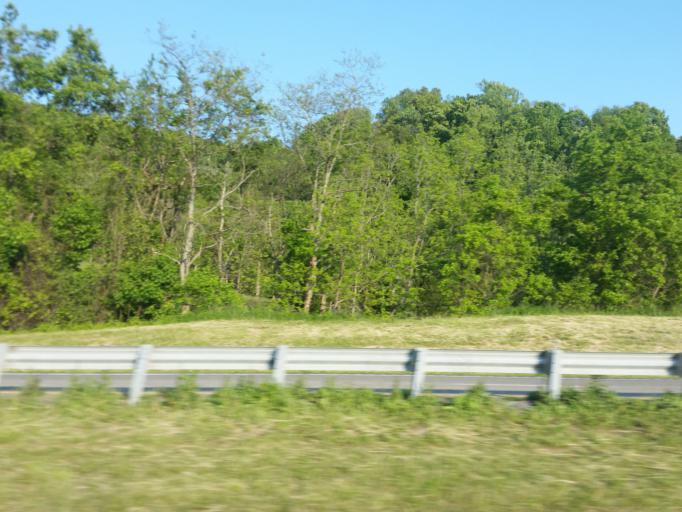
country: US
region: Virginia
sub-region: Russell County
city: Lebanon
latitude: 36.8847
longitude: -82.1050
